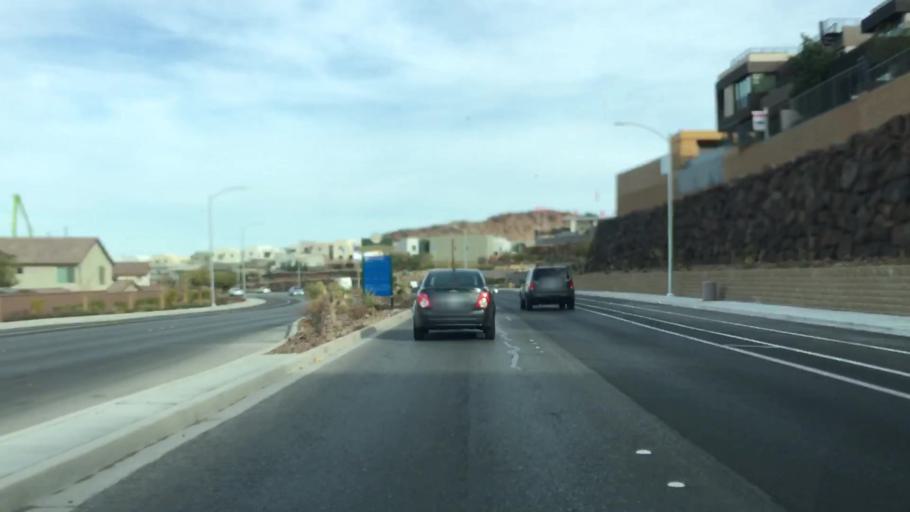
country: US
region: Nevada
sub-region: Clark County
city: Whitney
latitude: 35.9980
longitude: -115.0862
